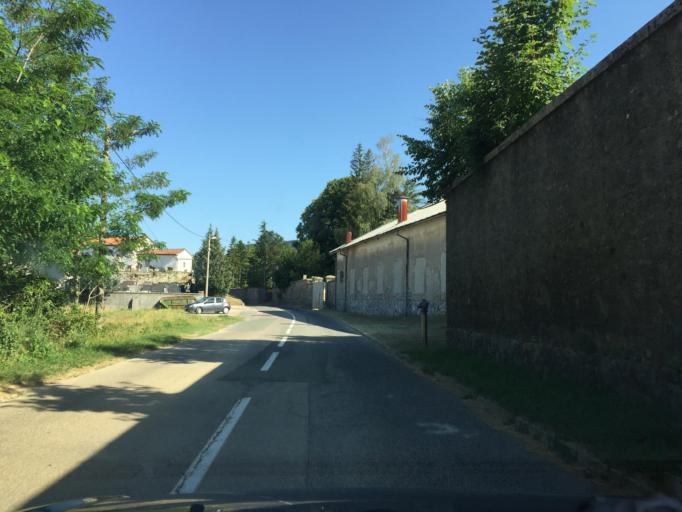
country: HR
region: Primorsko-Goranska
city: Klana
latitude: 45.4439
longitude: 14.3797
